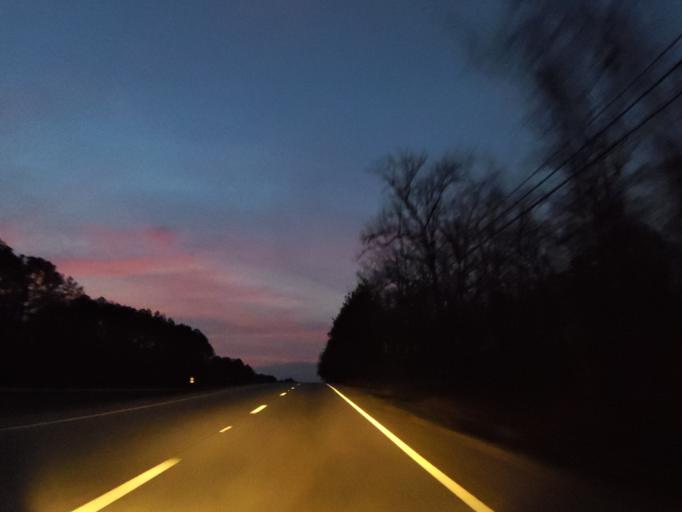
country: US
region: Tennessee
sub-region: Bradley County
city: East Cleveland
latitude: 35.1337
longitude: -84.7559
